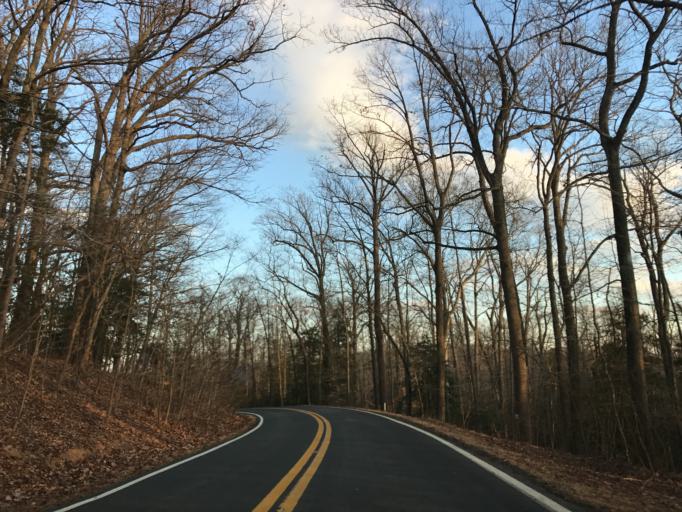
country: US
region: Maryland
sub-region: Cecil County
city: Charlestown
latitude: 39.4768
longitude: -75.9894
